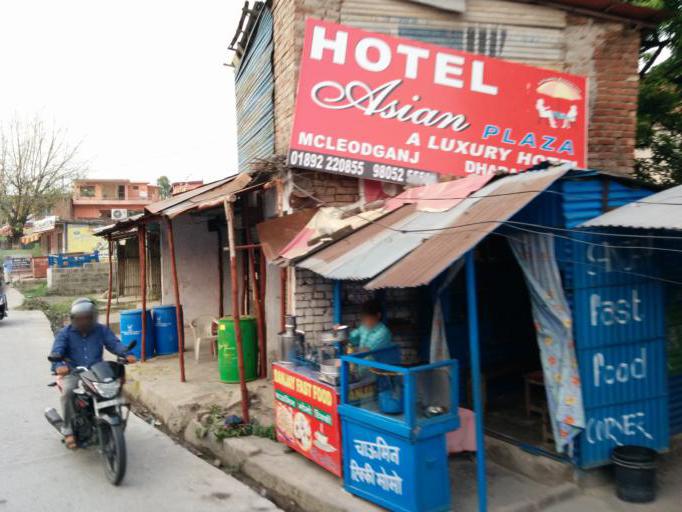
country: IN
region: Himachal Pradesh
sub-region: Kangra
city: Kangra
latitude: 32.1545
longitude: 76.2704
